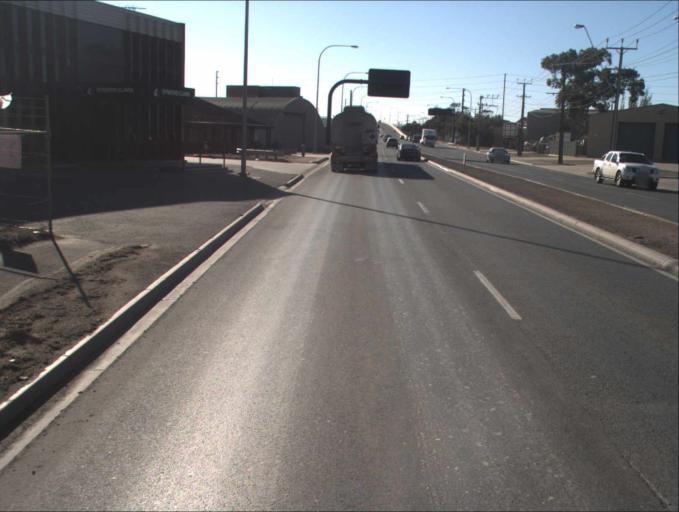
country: AU
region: South Australia
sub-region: Port Adelaide Enfield
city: Birkenhead
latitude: -34.8406
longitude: 138.5158
